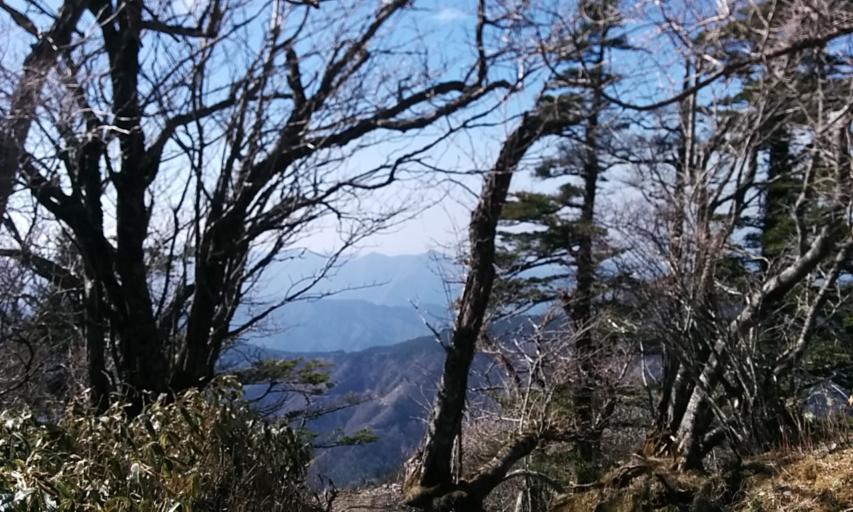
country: JP
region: Tokushima
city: Wakimachi
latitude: 33.8576
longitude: 134.0953
